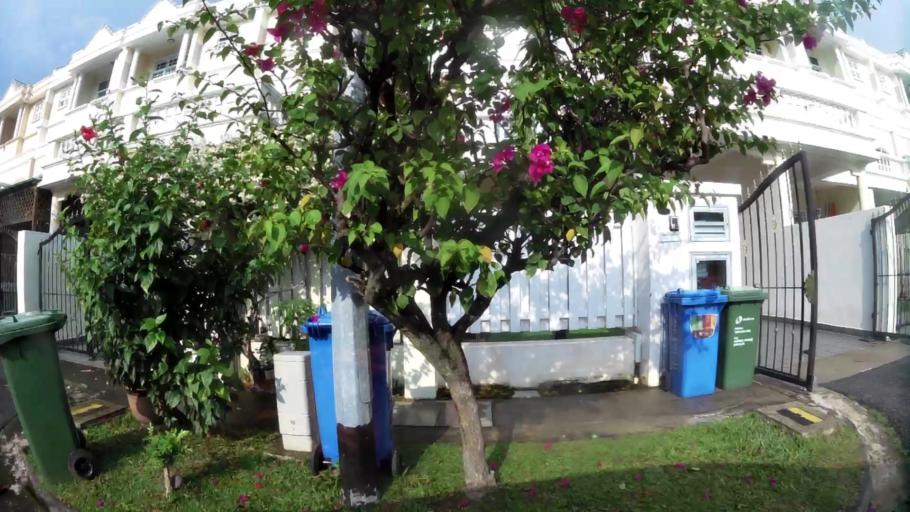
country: SG
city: Singapore
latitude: 1.3221
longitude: 103.9563
